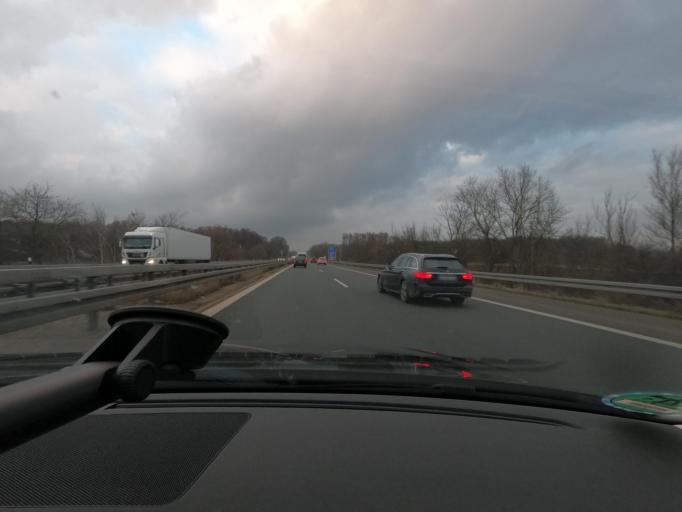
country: DE
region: Bavaria
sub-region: Regierungsbezirk Mittelfranken
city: Furth
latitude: 49.5301
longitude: 10.9925
